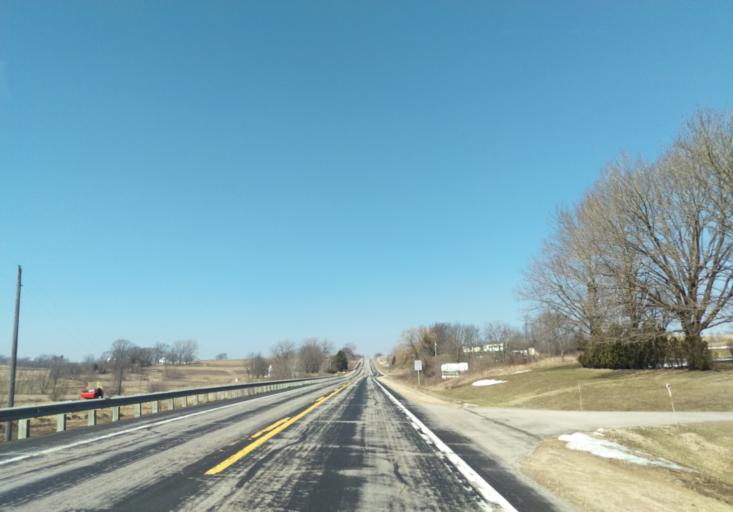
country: US
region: Wisconsin
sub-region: Vernon County
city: Viroqua
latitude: 43.5110
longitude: -90.8519
